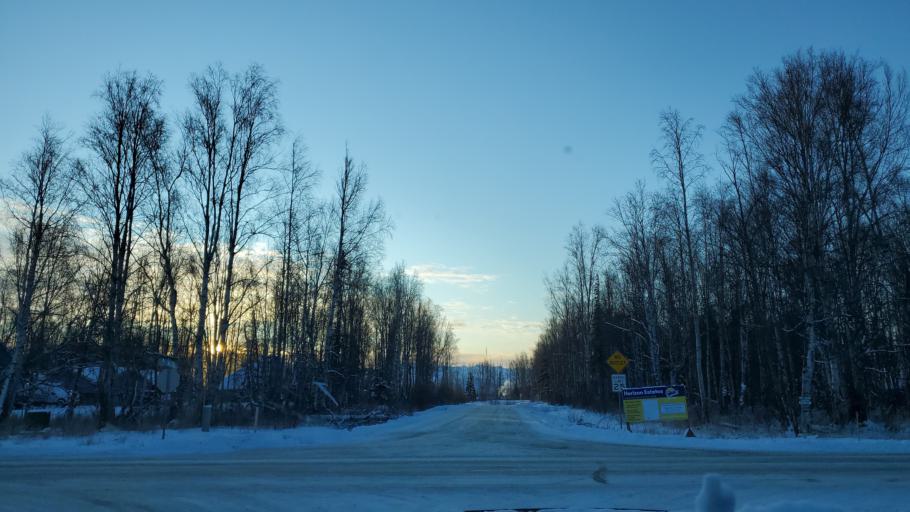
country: US
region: Alaska
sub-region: Matanuska-Susitna Borough
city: Lakes
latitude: 61.6357
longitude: -149.2950
